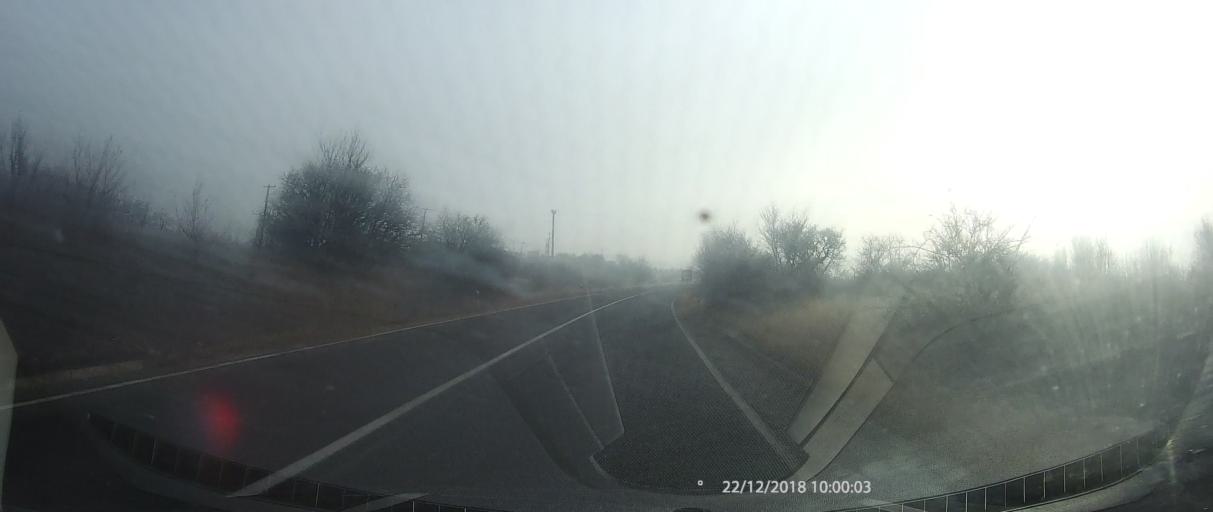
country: MK
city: Klechovce
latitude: 42.1492
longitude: 21.9729
